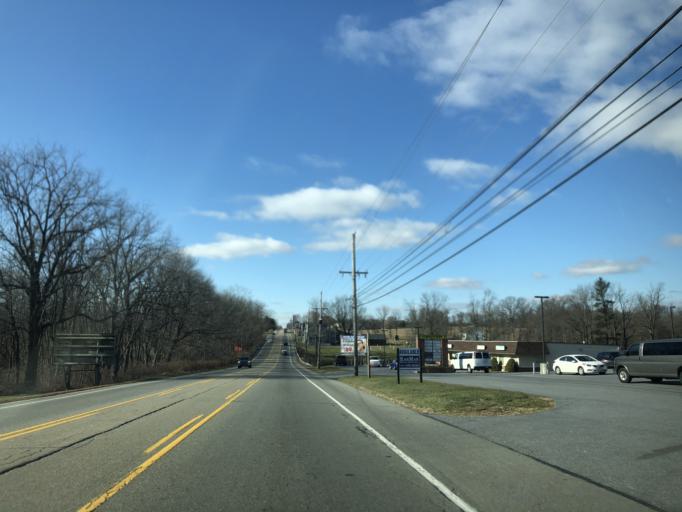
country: US
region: Pennsylvania
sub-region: Chester County
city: Parkesburg
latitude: 39.9847
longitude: -75.9430
